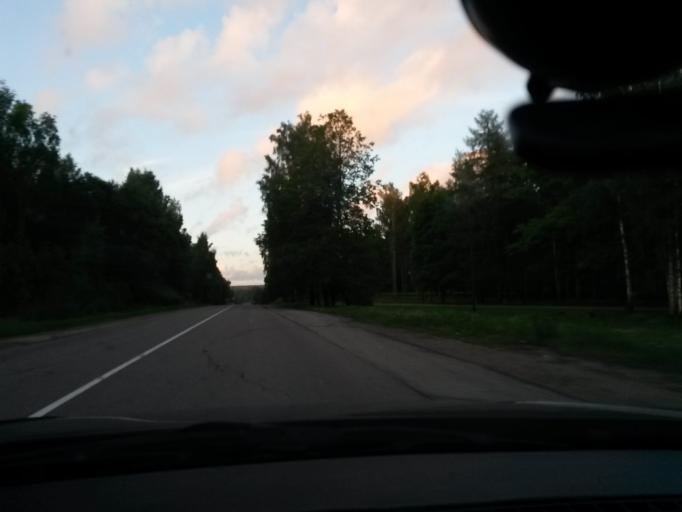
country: LV
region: Madonas Rajons
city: Madona
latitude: 56.8059
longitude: 26.0857
